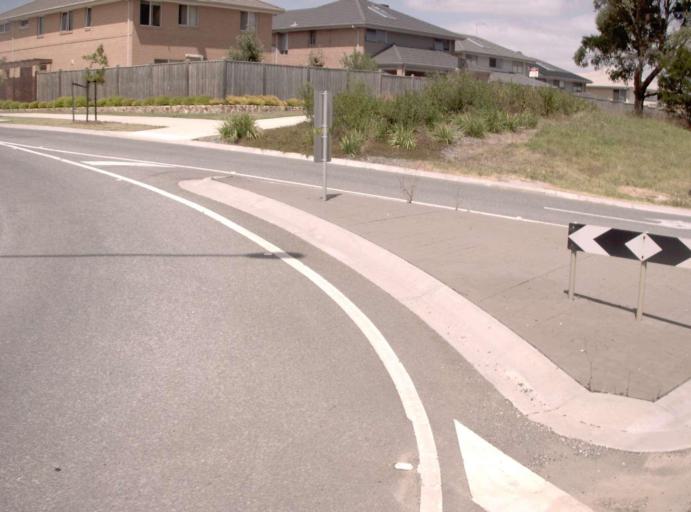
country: AU
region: Victoria
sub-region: Cardinia
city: Officer
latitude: -38.0646
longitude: 145.4301
